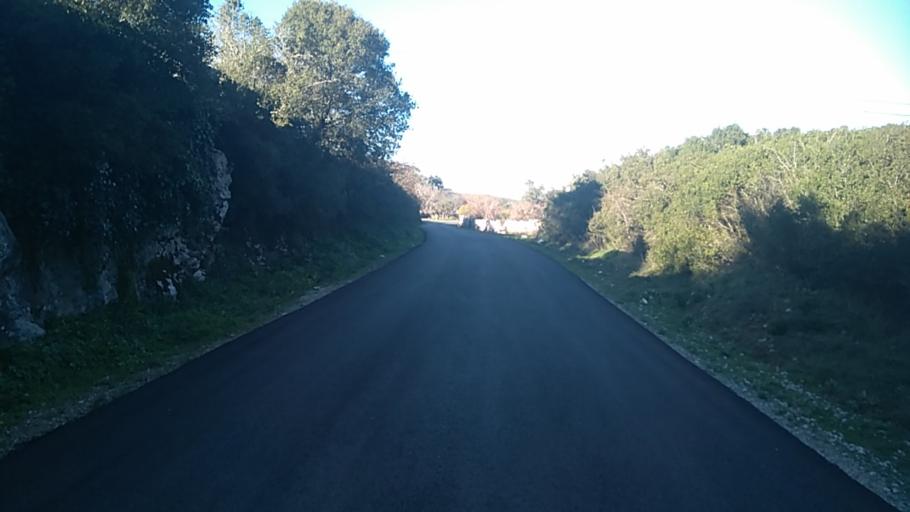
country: PT
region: Leiria
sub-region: Porto de Mos
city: Porto de Mos
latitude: 39.5507
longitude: -8.8444
